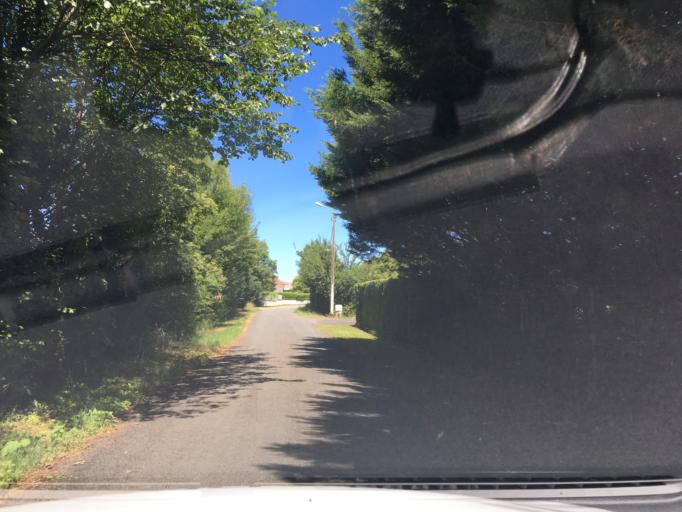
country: FR
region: Poitou-Charentes
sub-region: Departement des Deux-Sevres
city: Aiffres
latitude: 46.3147
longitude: -0.4234
